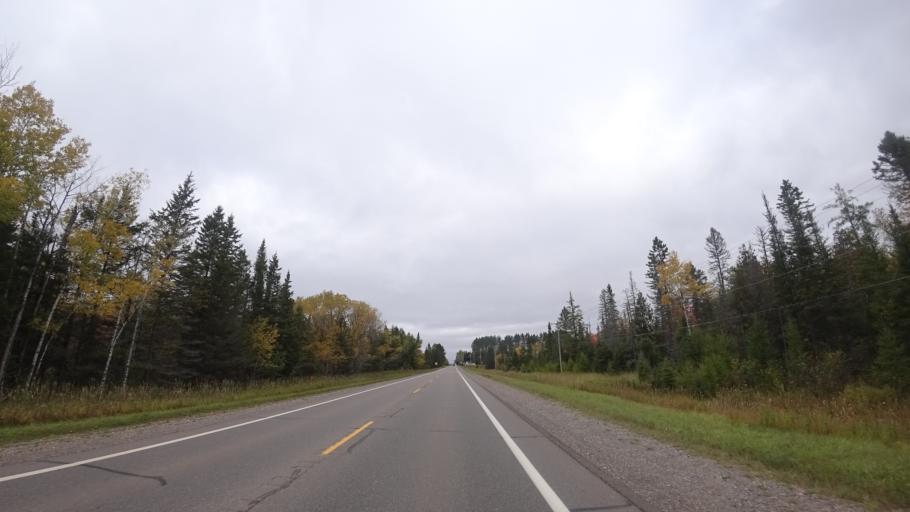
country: US
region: Michigan
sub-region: Iron County
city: Crystal Falls
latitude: 46.1316
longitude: -88.0923
